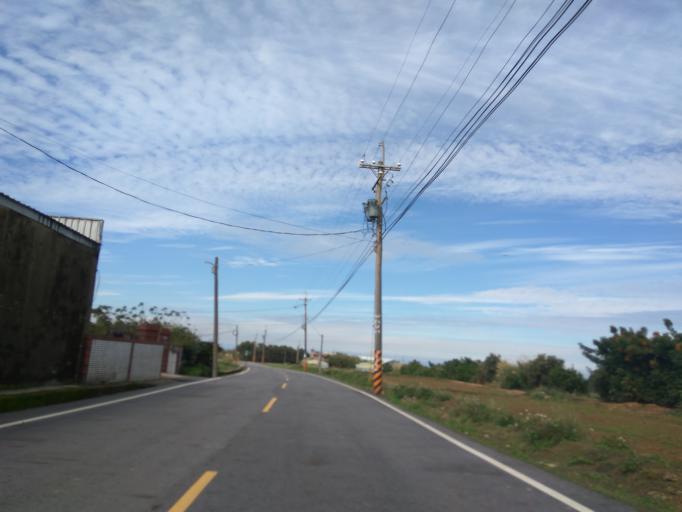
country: TW
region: Taiwan
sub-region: Hsinchu
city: Zhubei
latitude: 25.0040
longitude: 121.0829
